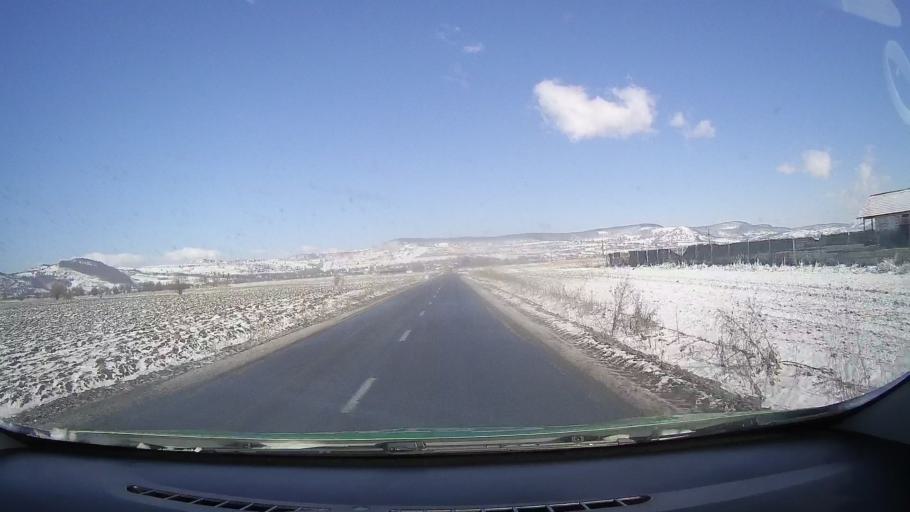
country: RO
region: Sibiu
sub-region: Comuna Avrig
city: Avrig
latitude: 45.7468
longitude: 24.3917
